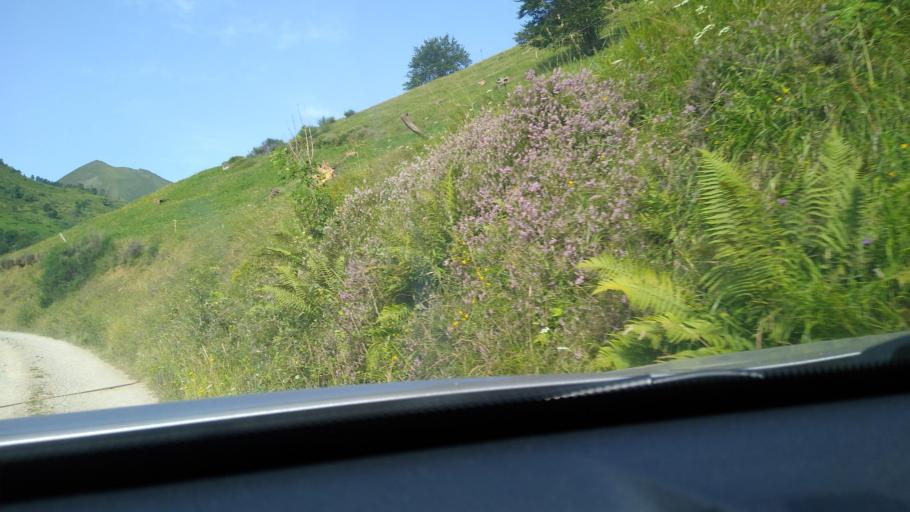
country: FR
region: Midi-Pyrenees
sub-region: Departement de l'Ariege
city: Saint-Girons
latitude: 42.7925
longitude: 1.1530
